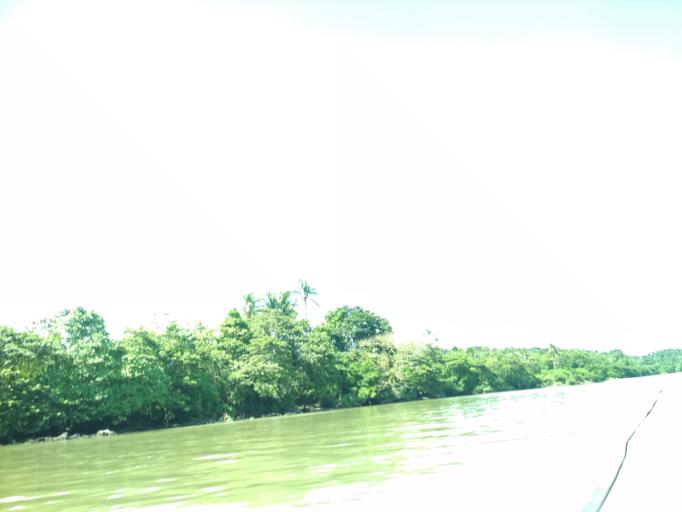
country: CO
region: Cauca
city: Timbiqui
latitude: 2.7656
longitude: -77.6631
